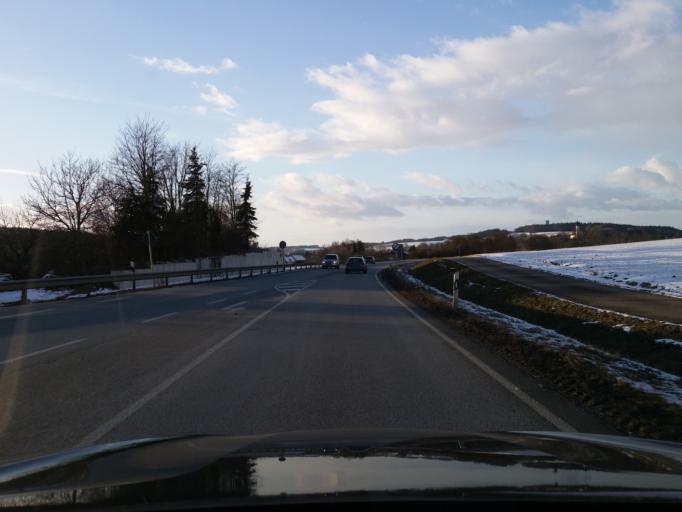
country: DE
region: Bavaria
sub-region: Lower Bavaria
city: Weihmichl
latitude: 48.5779
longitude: 12.0724
